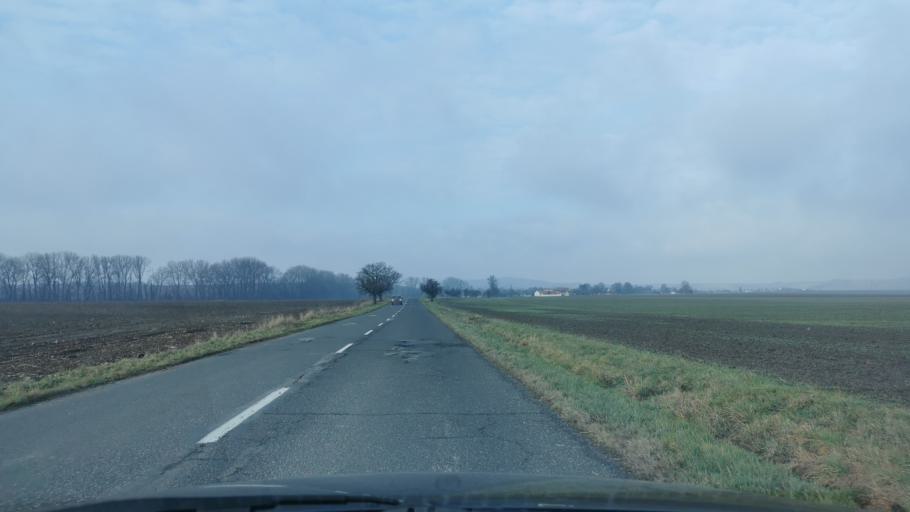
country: SK
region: Trnavsky
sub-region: Okres Senica
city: Senica
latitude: 48.6970
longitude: 17.3499
